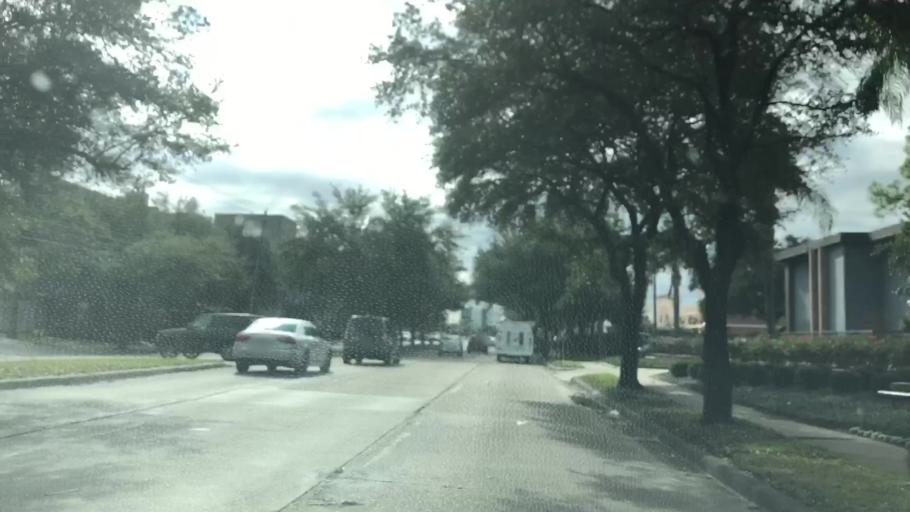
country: US
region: Texas
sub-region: Harris County
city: Piney Point Village
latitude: 29.7415
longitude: -95.5010
